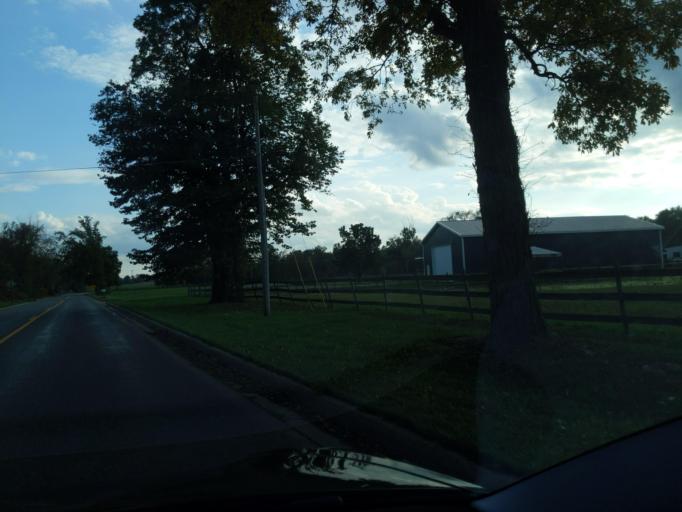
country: US
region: Michigan
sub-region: Jackson County
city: Jackson
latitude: 42.2896
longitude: -84.4626
